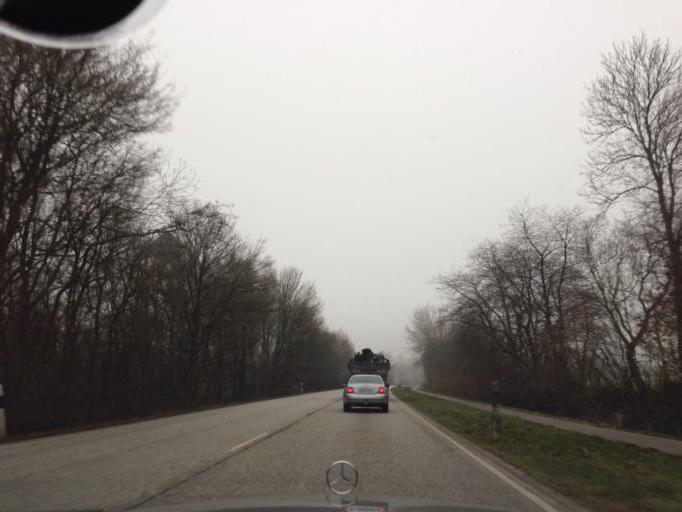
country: DE
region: Schleswig-Holstein
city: Klein Barkau
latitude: 54.2492
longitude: 10.1490
